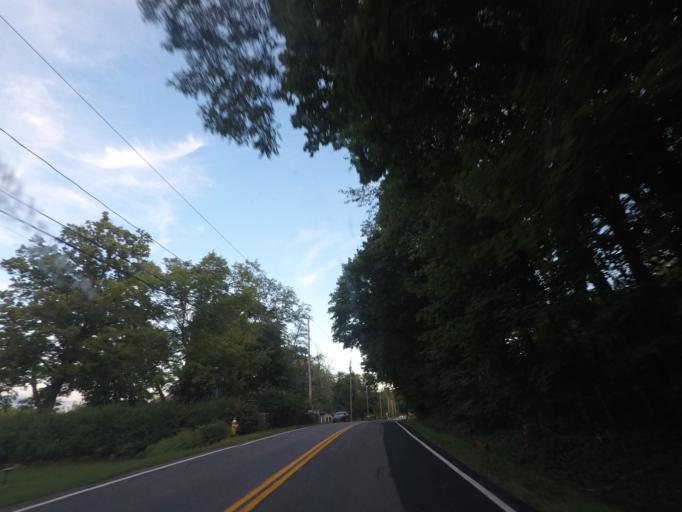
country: US
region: New York
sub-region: Schenectady County
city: Niskayuna
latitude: 42.7750
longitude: -73.8211
